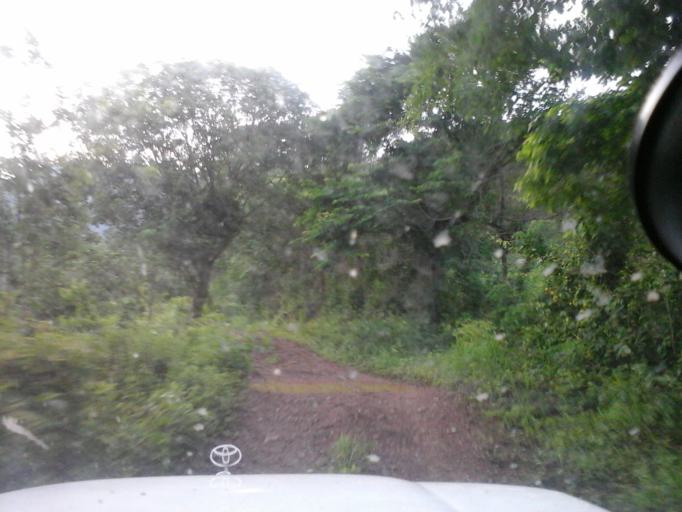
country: CO
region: Cesar
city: Agustin Codazzi
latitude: 10.1738
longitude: -73.1479
